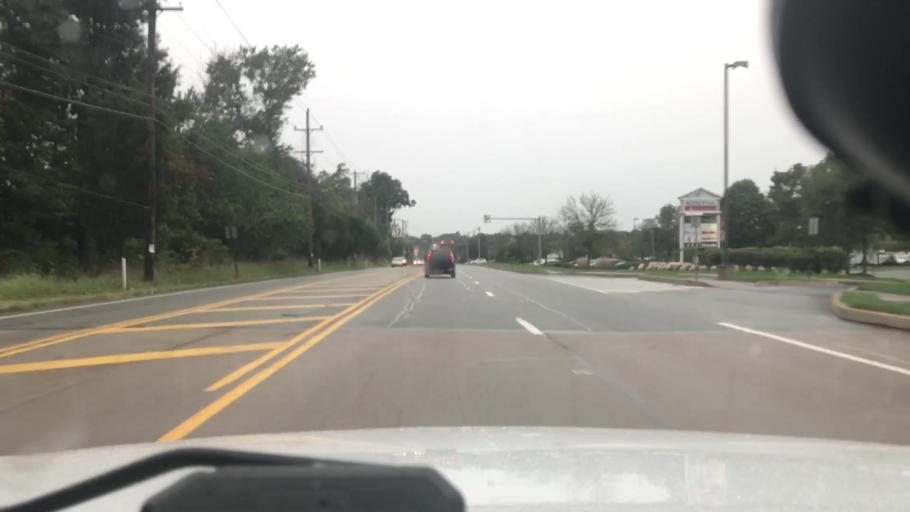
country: US
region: Pennsylvania
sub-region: Montgomery County
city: Montgomeryville
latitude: 40.2241
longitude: -75.2545
